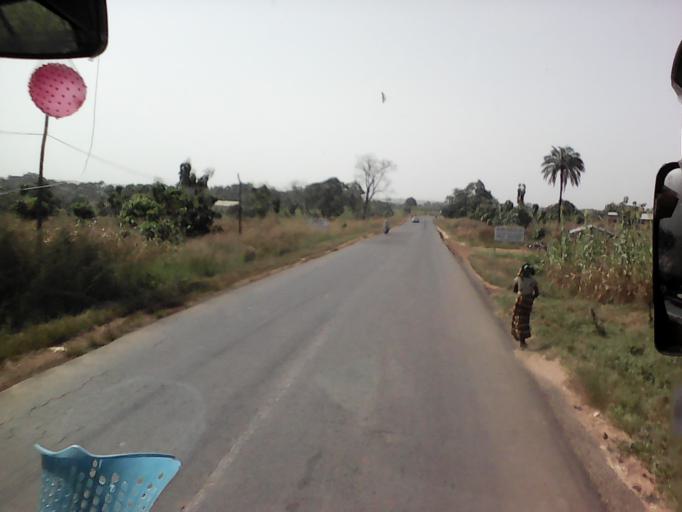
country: TG
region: Centrale
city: Sokode
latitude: 8.9462
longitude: 1.1298
